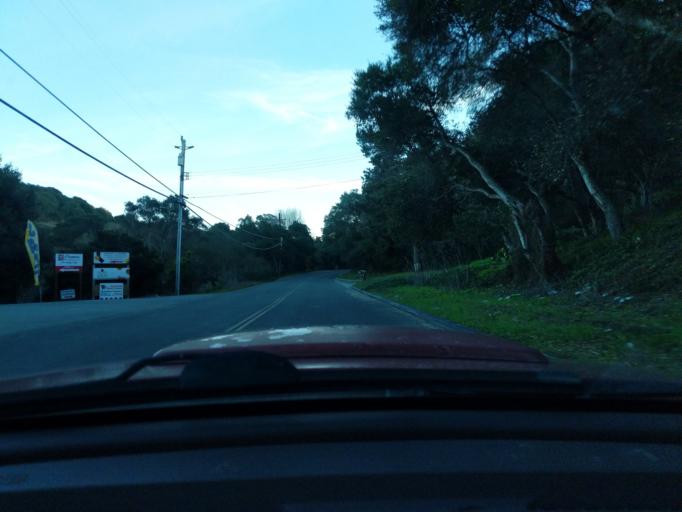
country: US
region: California
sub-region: San Benito County
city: Aromas
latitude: 36.8557
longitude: -121.6822
